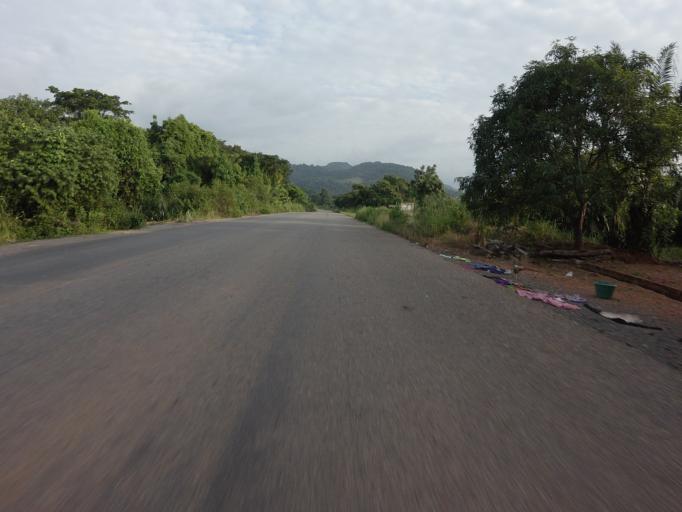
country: GH
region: Volta
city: Kpandu
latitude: 6.8805
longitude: 0.4208
